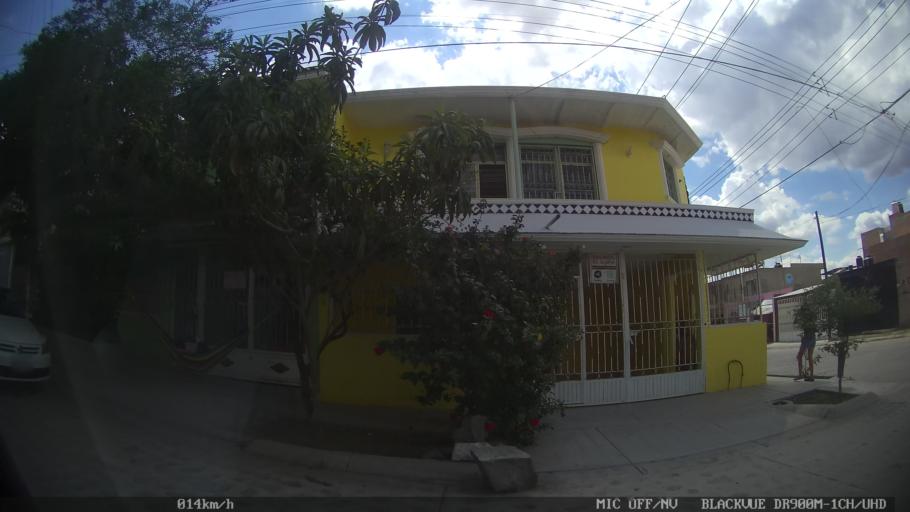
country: MX
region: Jalisco
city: Tlaquepaque
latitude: 20.6723
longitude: -103.2586
